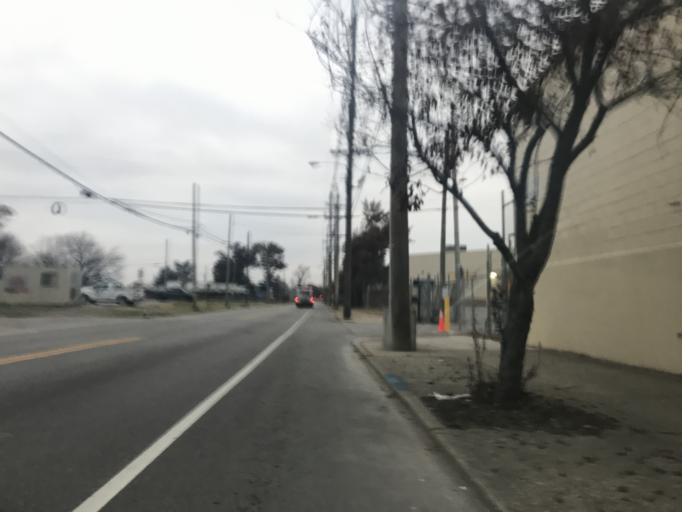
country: US
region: Kentucky
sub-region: Jefferson County
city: Louisville
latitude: 38.2330
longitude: -85.7742
